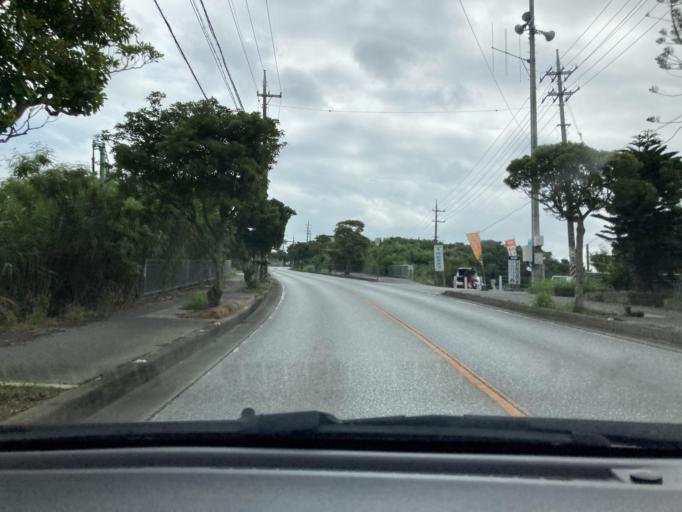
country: JP
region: Okinawa
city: Ginowan
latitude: 26.2598
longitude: 127.7765
